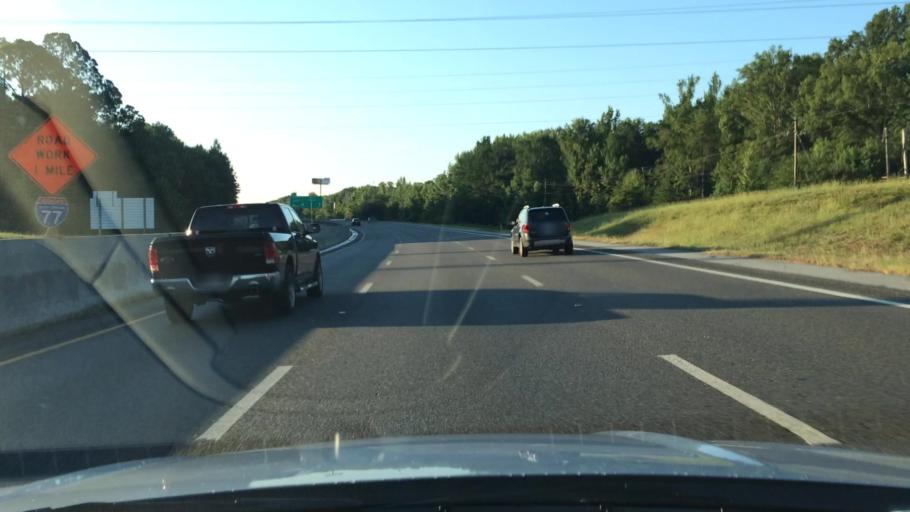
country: US
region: South Carolina
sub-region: Lexington County
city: Cayce
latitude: 33.9385
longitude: -81.0863
